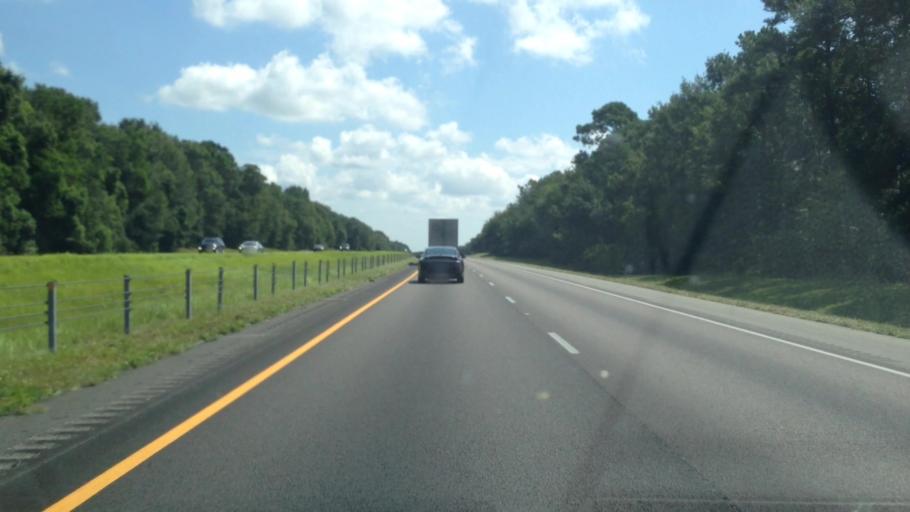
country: US
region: Alabama
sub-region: Mobile County
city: Grand Bay
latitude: 30.5035
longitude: -88.3054
